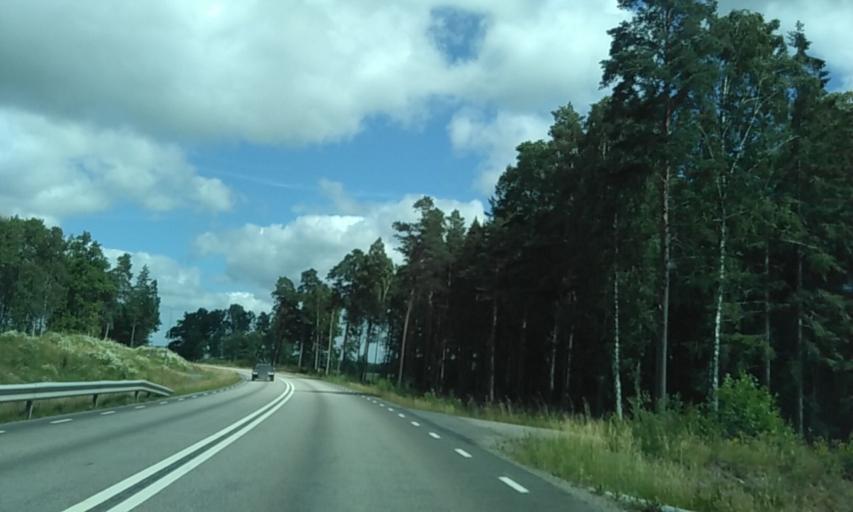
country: SE
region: Vaestra Goetaland
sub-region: Grastorps Kommun
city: Graestorp
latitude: 58.3241
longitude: 12.6861
